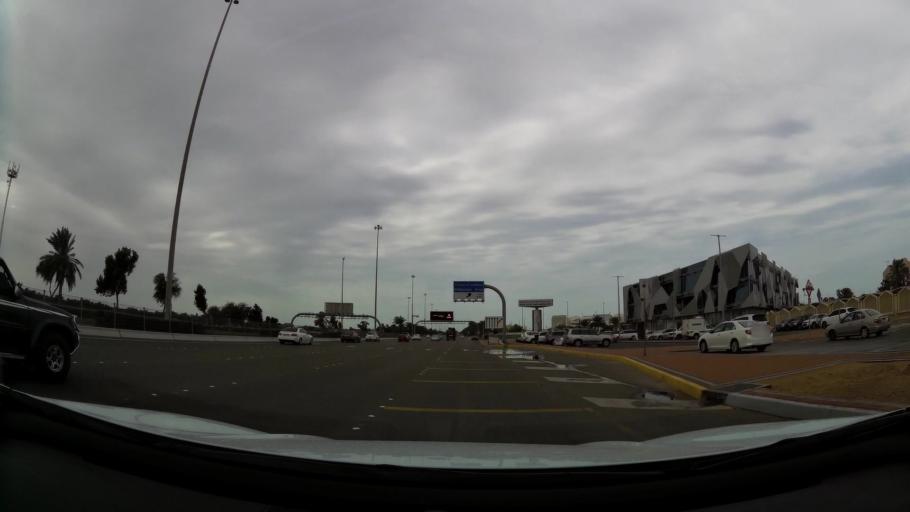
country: AE
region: Abu Dhabi
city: Abu Dhabi
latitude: 24.4195
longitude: 54.4289
